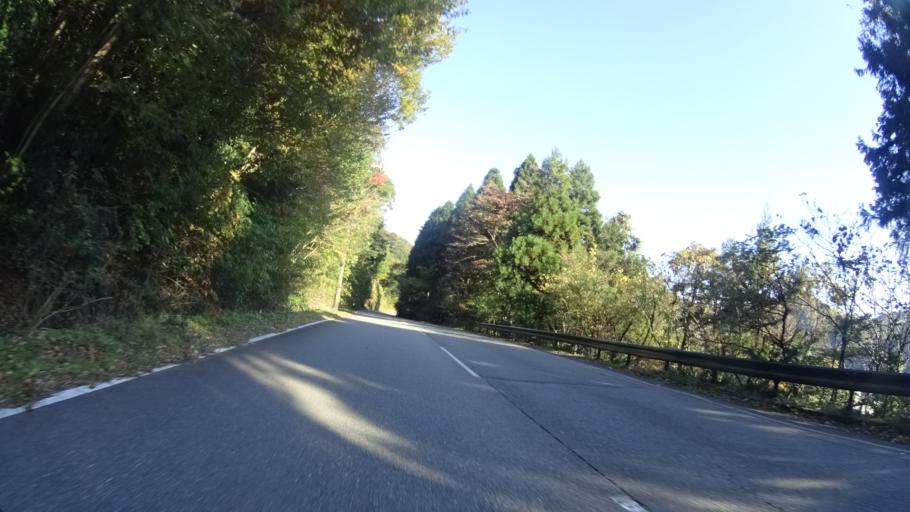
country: JP
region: Fukui
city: Maruoka
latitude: 36.2454
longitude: 136.3713
